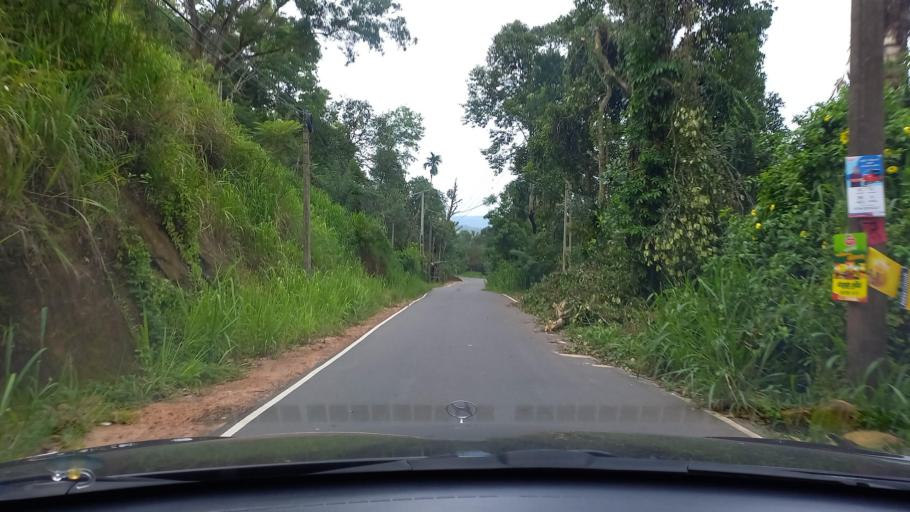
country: LK
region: Central
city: Gampola
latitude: 7.2236
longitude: 80.6068
